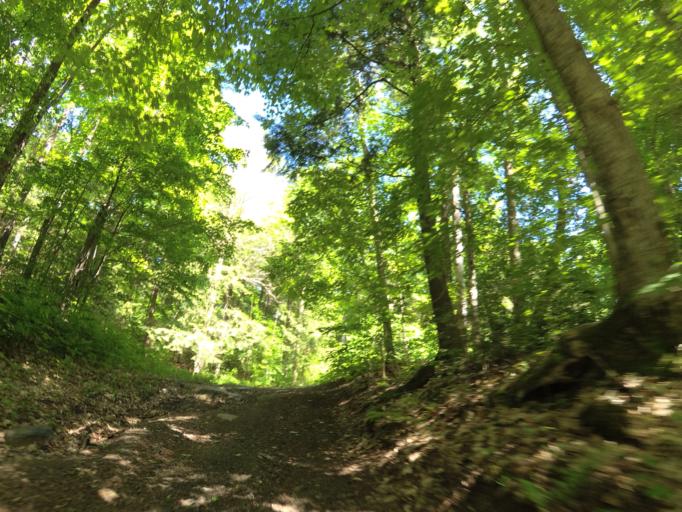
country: CA
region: Ontario
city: Renfrew
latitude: 45.0438
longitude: -76.8395
